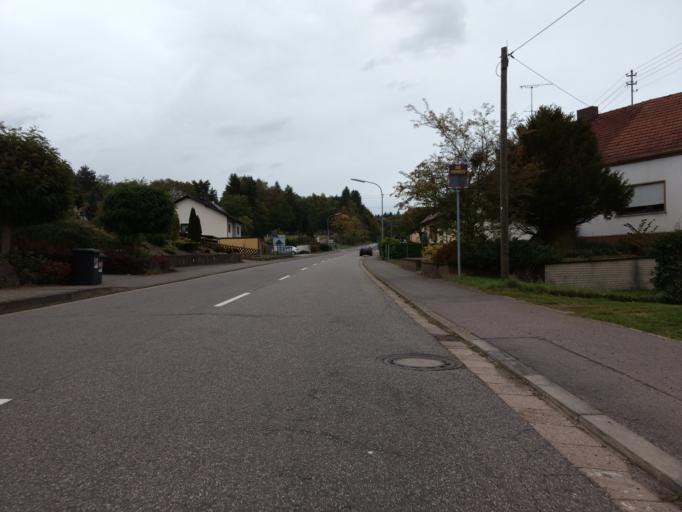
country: DE
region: Saarland
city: Losheim
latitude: 49.4557
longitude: 6.7860
